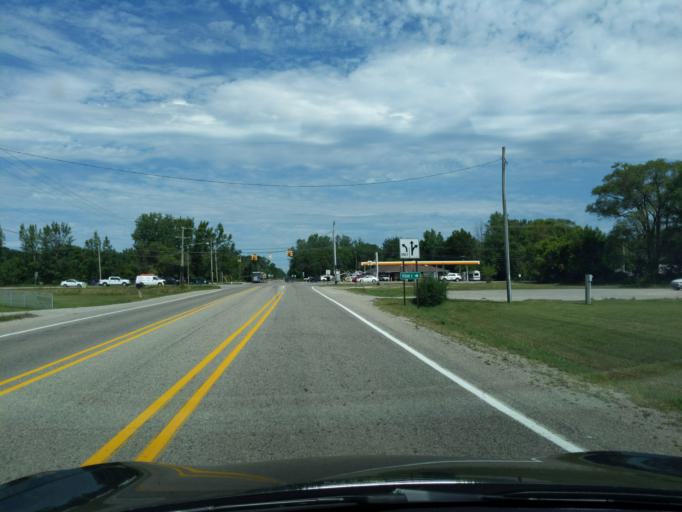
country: US
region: Michigan
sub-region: Midland County
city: Midland
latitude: 43.6114
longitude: -84.3692
